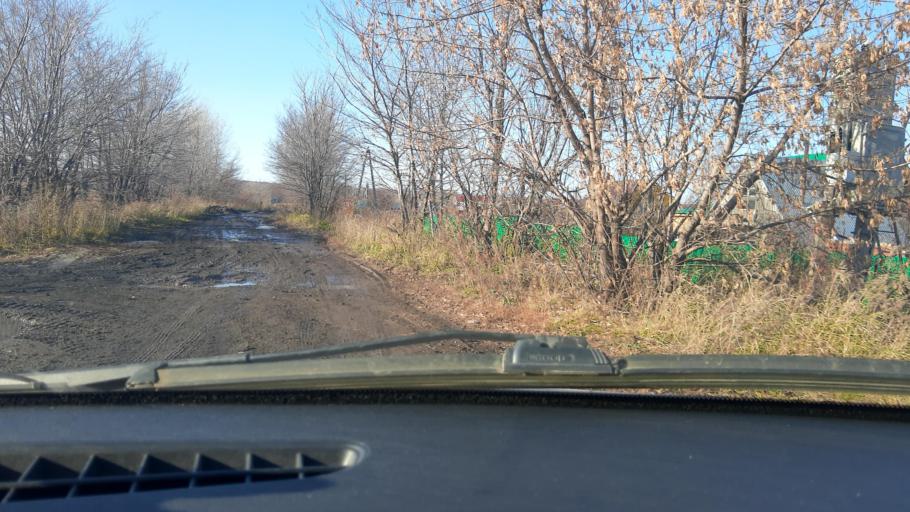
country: RU
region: Bashkortostan
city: Avdon
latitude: 54.7160
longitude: 55.7868
